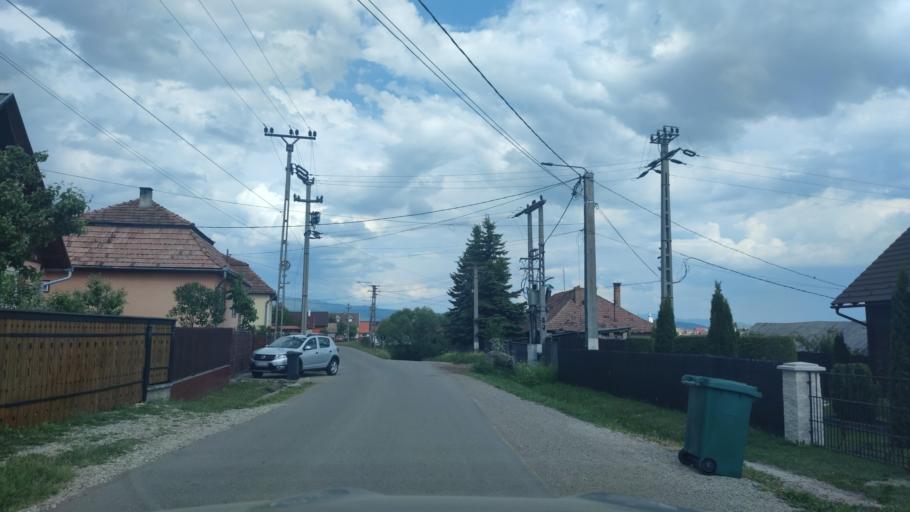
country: RO
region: Harghita
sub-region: Comuna Remetea
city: Remetea
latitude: 46.7955
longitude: 25.4446
